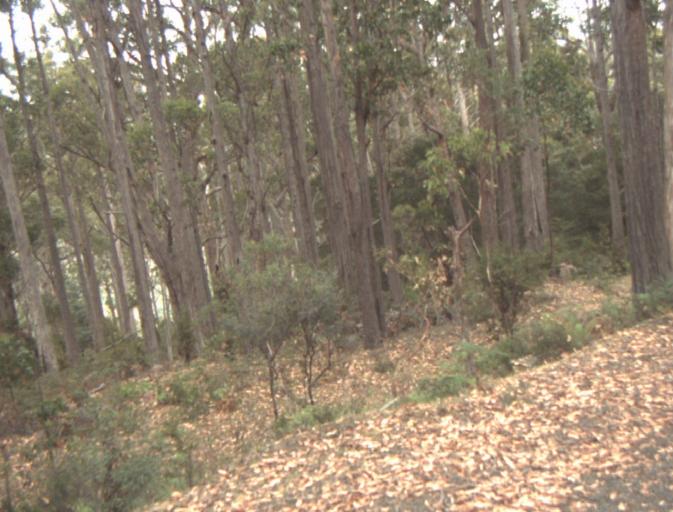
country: AU
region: Tasmania
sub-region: Northern Midlands
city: Evandale
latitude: -41.4946
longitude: 147.5504
